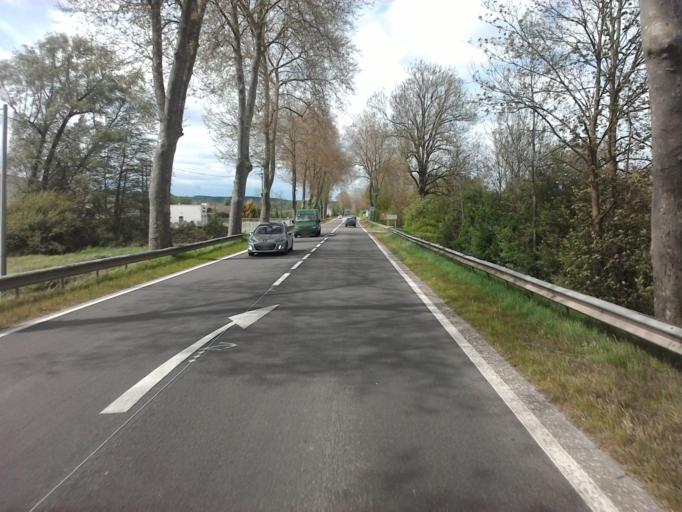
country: FR
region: Bourgogne
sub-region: Departement de l'Yonne
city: Champs-sur-Yonne
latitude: 47.7181
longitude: 3.6147
